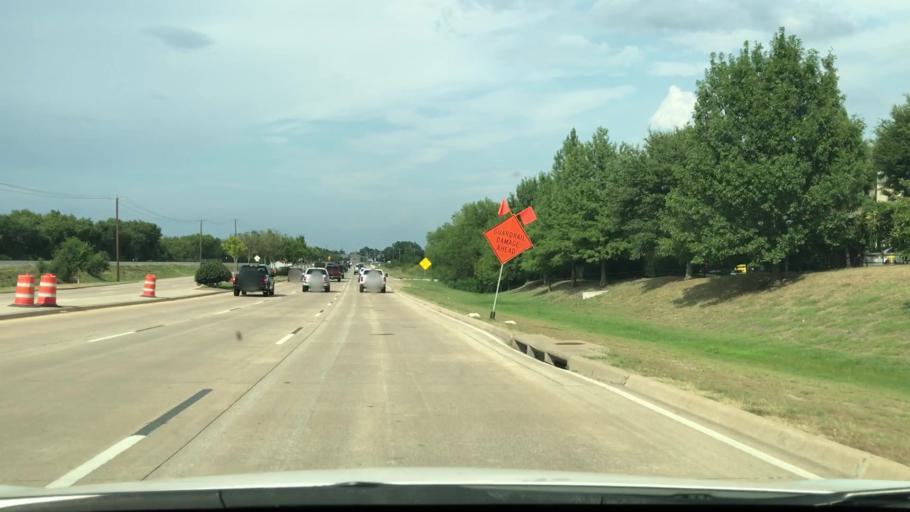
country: US
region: Texas
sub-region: Dallas County
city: Sachse
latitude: 32.9938
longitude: -96.5678
